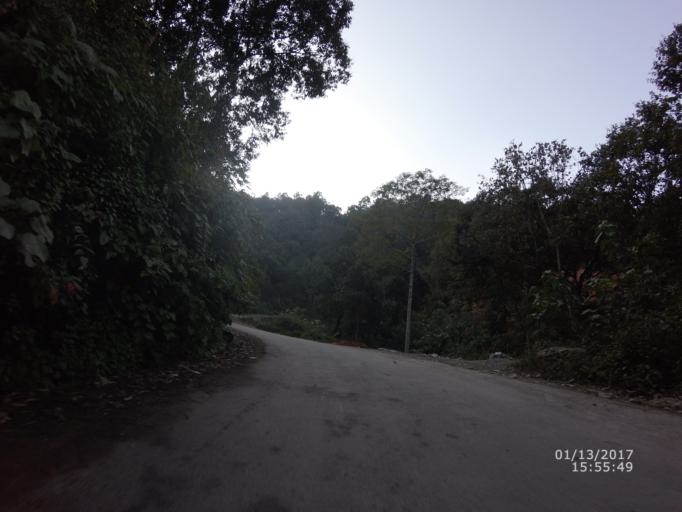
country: NP
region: Western Region
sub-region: Gandaki Zone
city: Pokhara
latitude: 28.1576
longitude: 84.0032
